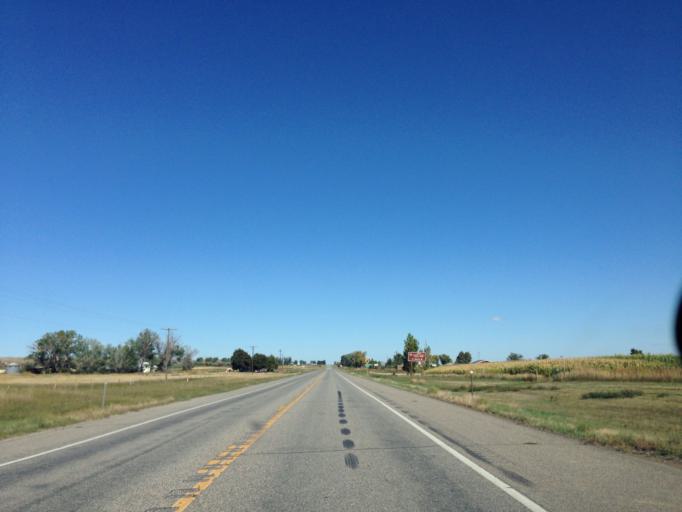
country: US
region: Montana
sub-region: Yellowstone County
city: Laurel
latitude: 45.4614
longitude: -108.8629
